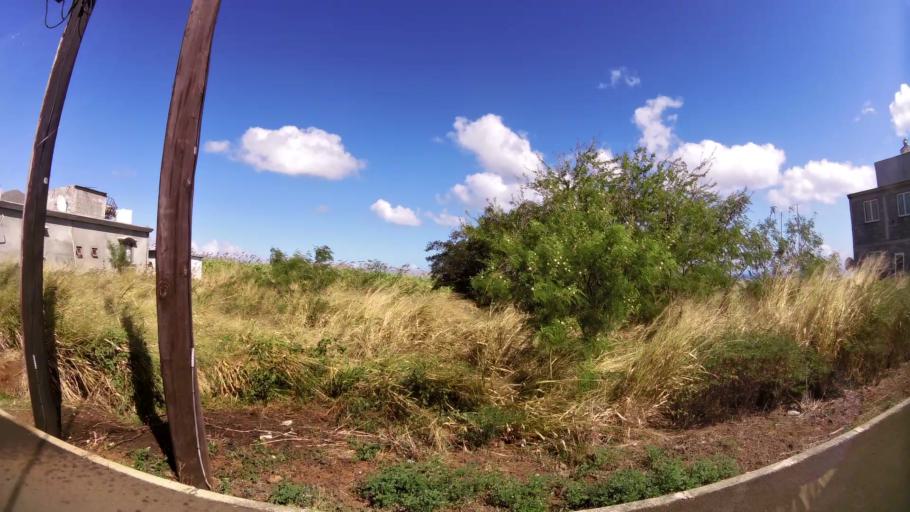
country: MU
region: Black River
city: Cascavelle
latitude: -20.2686
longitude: 57.4135
